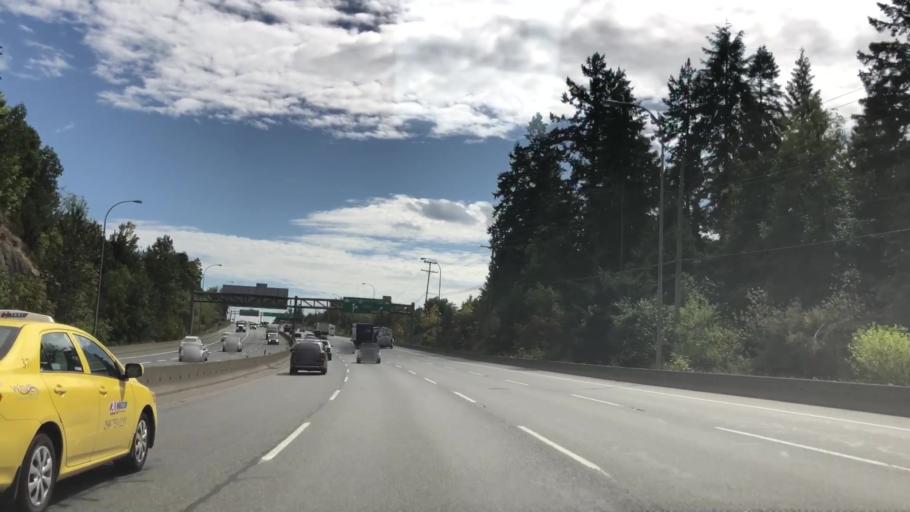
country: CA
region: British Columbia
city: Nanaimo
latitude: 49.1192
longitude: -123.9130
